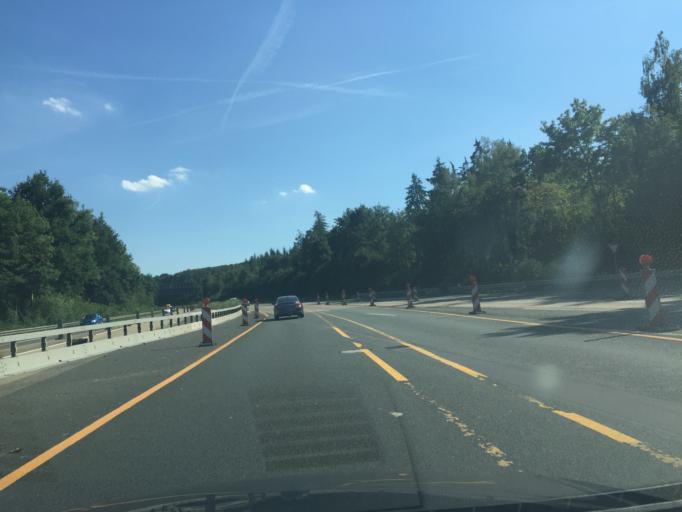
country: DE
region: Hesse
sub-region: Regierungsbezirk Giessen
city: Wetzlar
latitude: 50.5682
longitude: 8.5479
